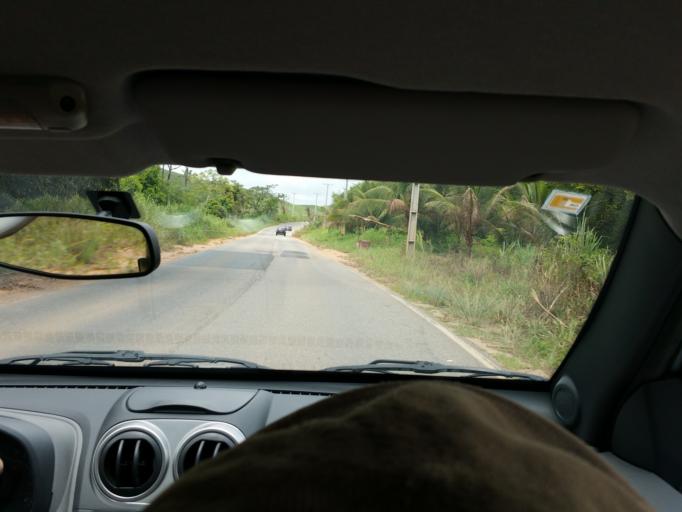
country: BR
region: Pernambuco
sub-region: Sirinhaem
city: Sirinhaem
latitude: -8.6241
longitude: -35.1246
